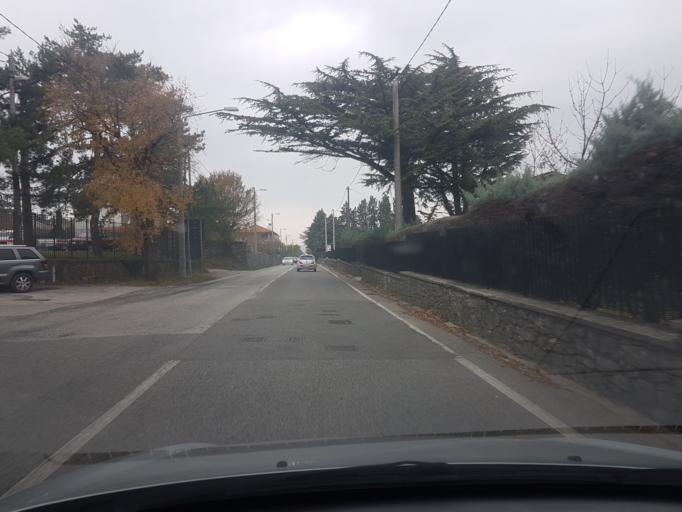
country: IT
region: Friuli Venezia Giulia
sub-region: Provincia di Trieste
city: Santa Croce
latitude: 45.7374
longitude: 13.6907
